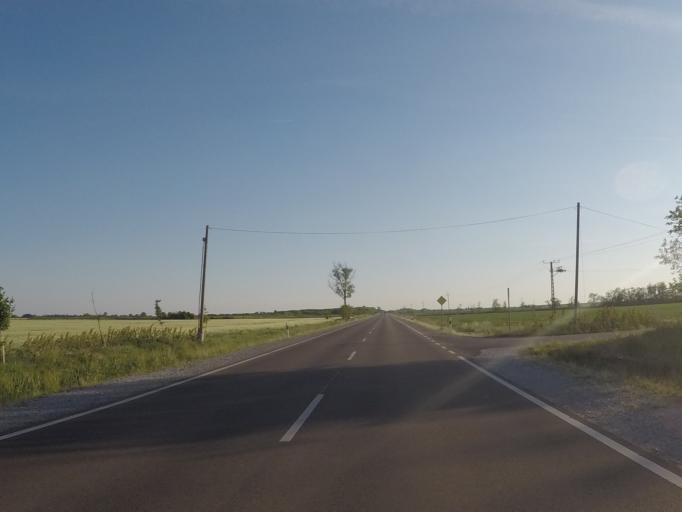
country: HU
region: Heves
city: Erdotelek
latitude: 47.6774
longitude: 20.3759
